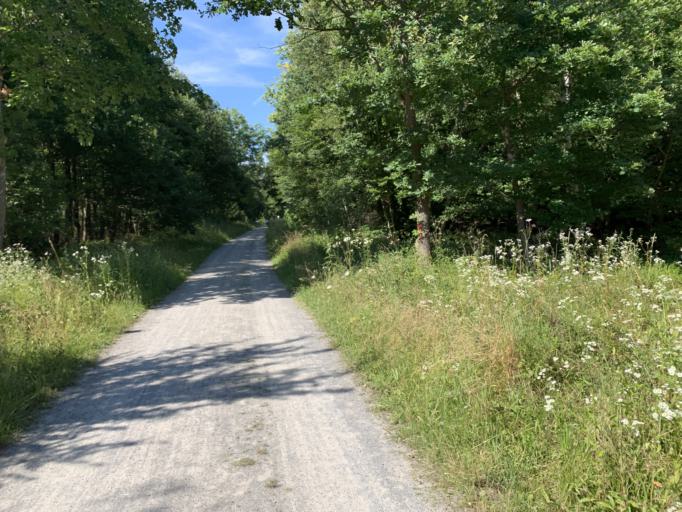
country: DE
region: Baden-Wuerttemberg
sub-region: Karlsruhe Region
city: Tiefenbronn
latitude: 48.8345
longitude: 8.7989
